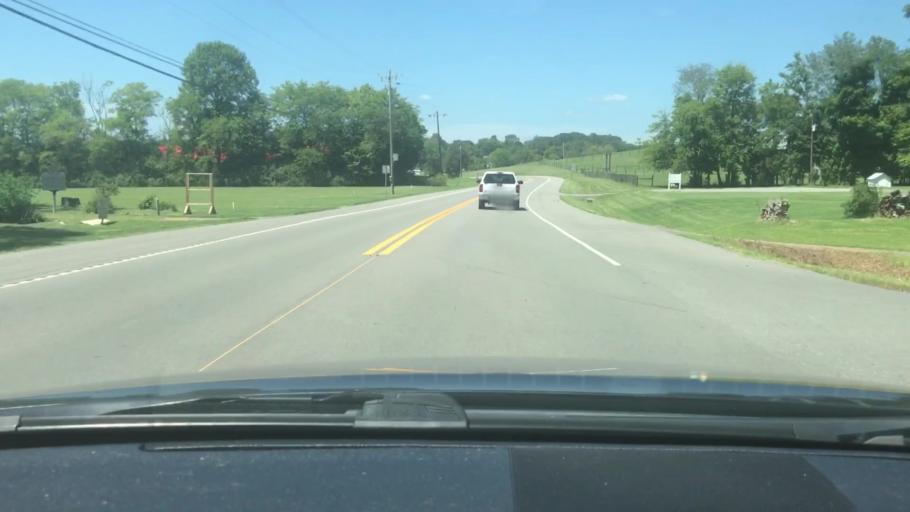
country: US
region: Tennessee
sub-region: Sumner County
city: Gallatin
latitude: 36.4517
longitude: -86.5380
